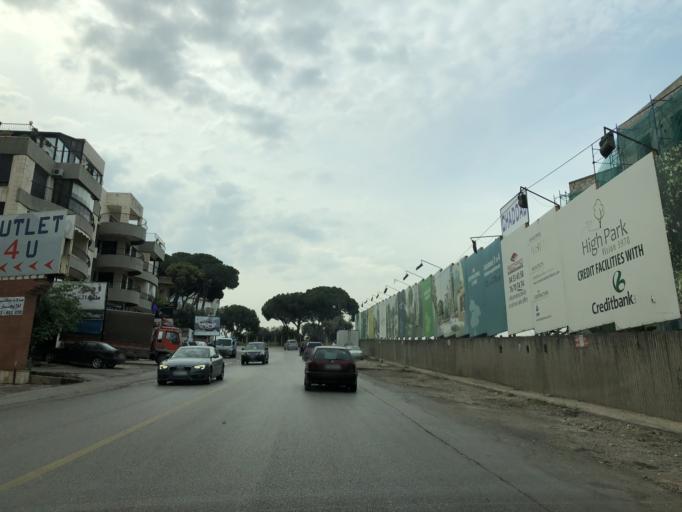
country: LB
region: Mont-Liban
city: Jdaidet el Matn
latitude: 33.8558
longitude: 35.5827
